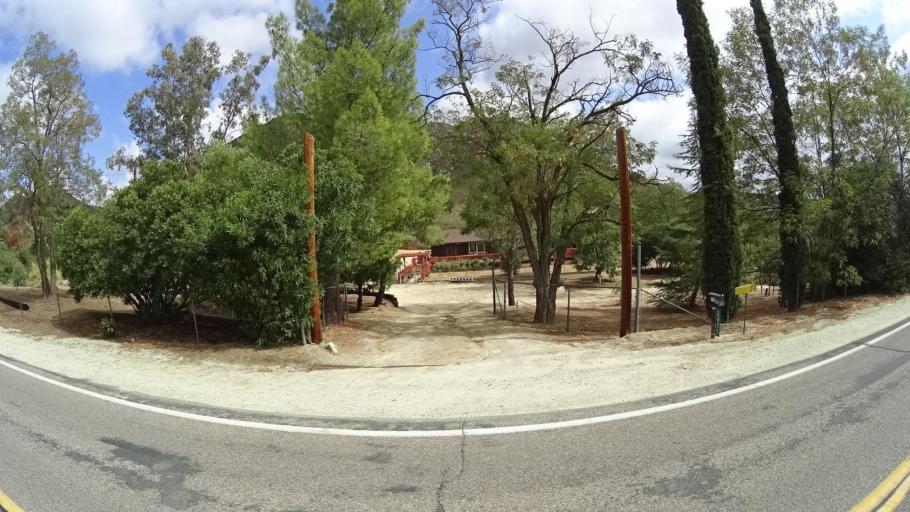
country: US
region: California
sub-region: San Diego County
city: Campo
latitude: 32.6815
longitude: -116.4889
